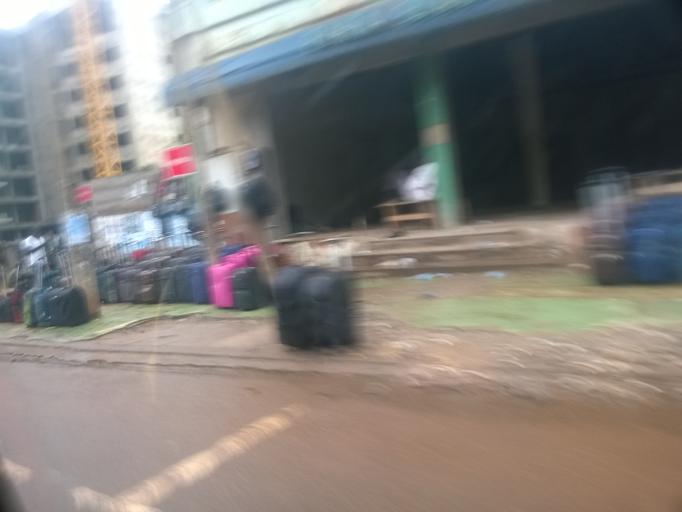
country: CM
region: Centre
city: Yaounde
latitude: 3.8681
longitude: 11.5215
